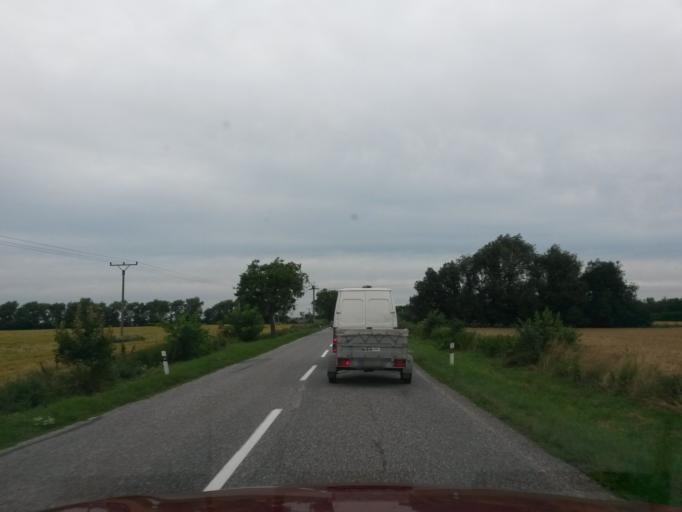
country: SK
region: Nitriansky
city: Levice
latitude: 48.1403
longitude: 18.5853
